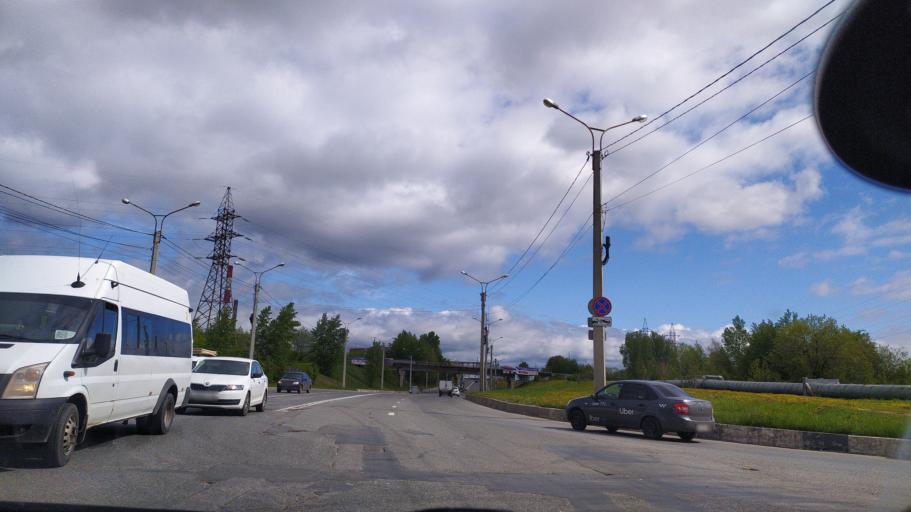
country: RU
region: Chuvashia
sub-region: Cheboksarskiy Rayon
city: Cheboksary
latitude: 56.1114
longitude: 47.2957
